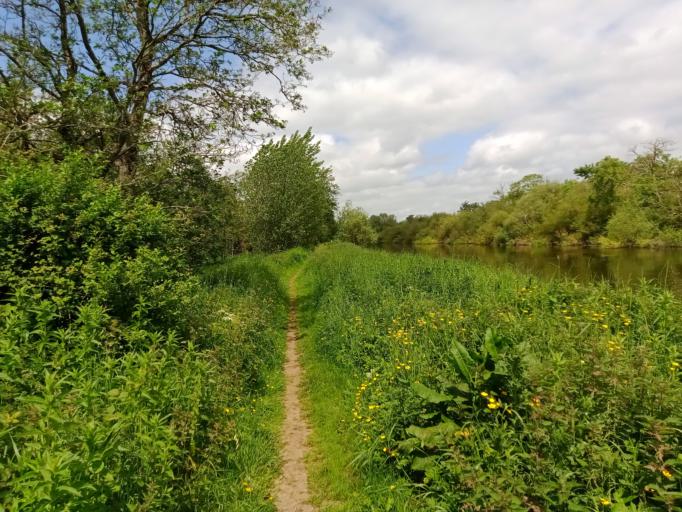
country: IE
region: Leinster
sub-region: County Carlow
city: Carlow
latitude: 52.7943
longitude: -6.9608
